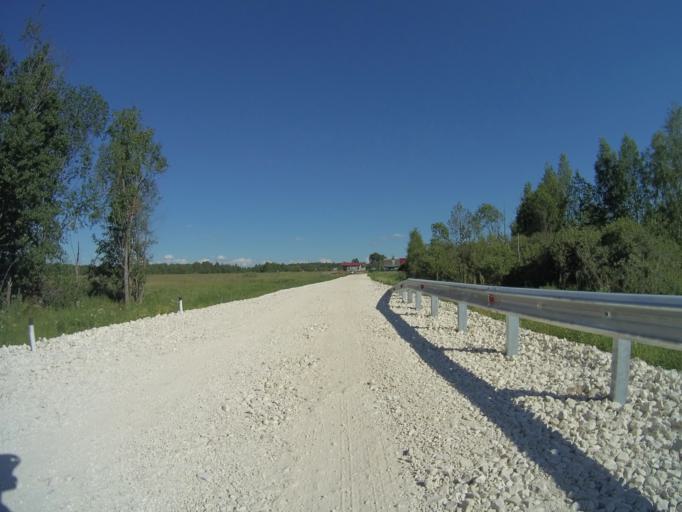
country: RU
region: Vladimir
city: Raduzhnyy
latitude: 56.0058
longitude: 40.3905
